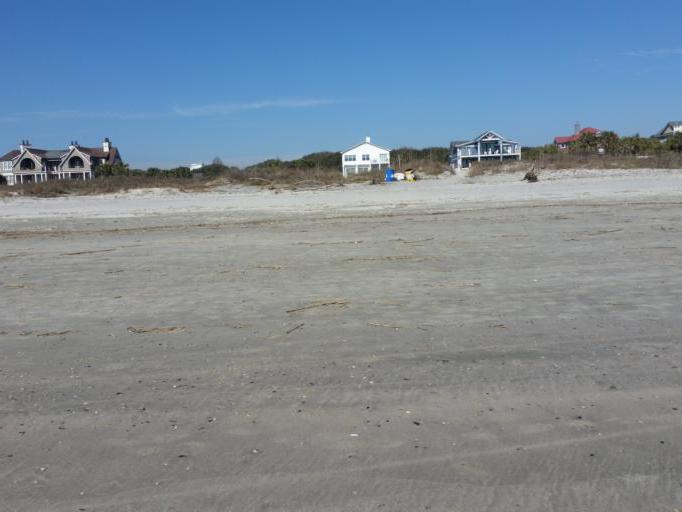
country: US
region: South Carolina
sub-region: Charleston County
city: Isle of Palms
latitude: 32.7952
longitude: -79.7601
